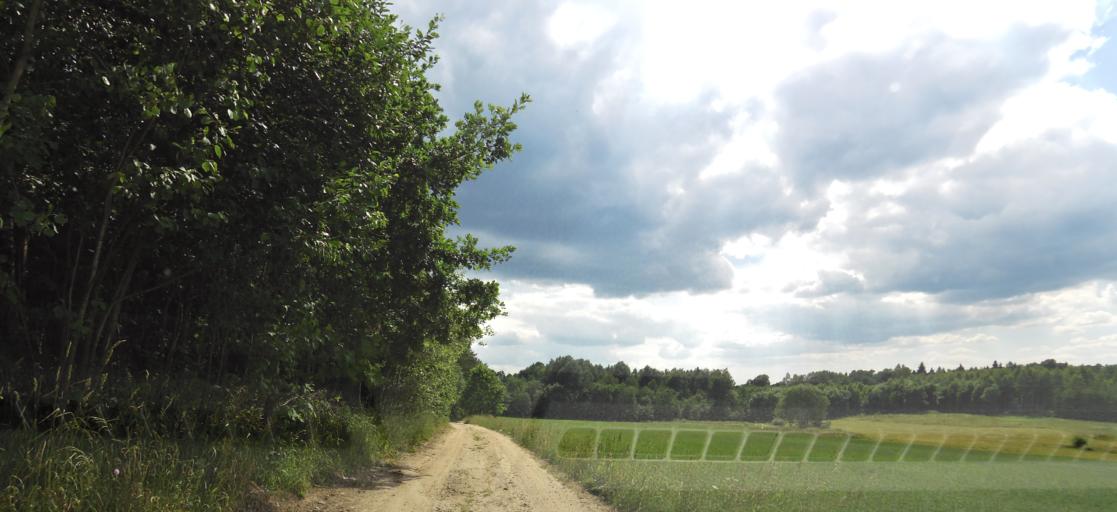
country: LT
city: Skaidiskes
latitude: 54.5278
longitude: 25.6226
